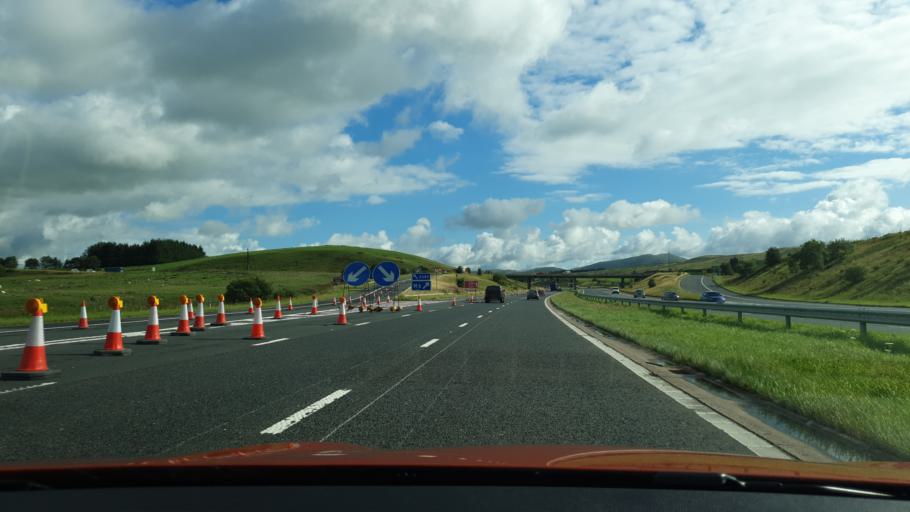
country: GB
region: England
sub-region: Cumbria
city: Sedbergh
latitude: 54.3284
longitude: -2.6267
